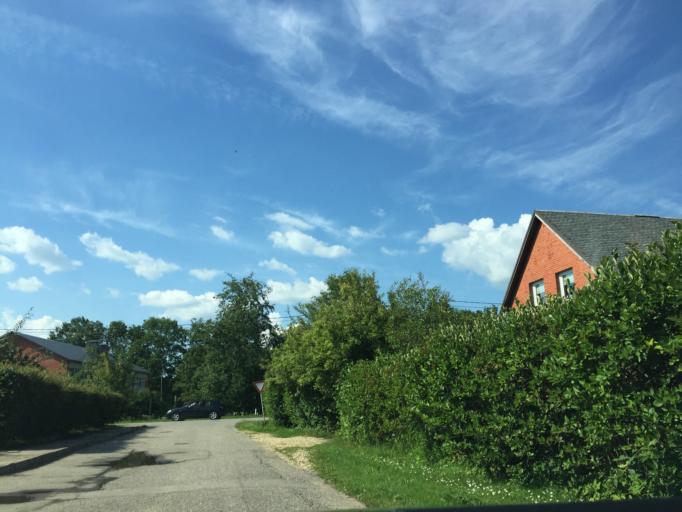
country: LV
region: Sigulda
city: Sigulda
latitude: 57.1525
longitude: 24.8625
